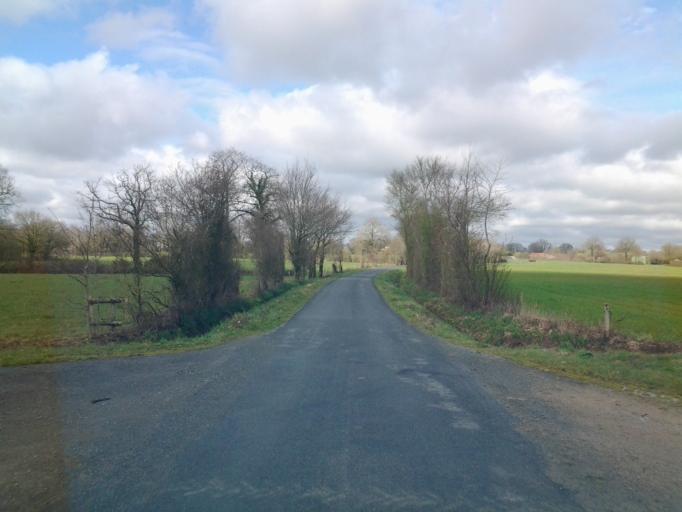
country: FR
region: Pays de la Loire
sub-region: Departement de la Vendee
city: La Chaize-le-Vicomte
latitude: 46.6537
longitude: -1.3564
